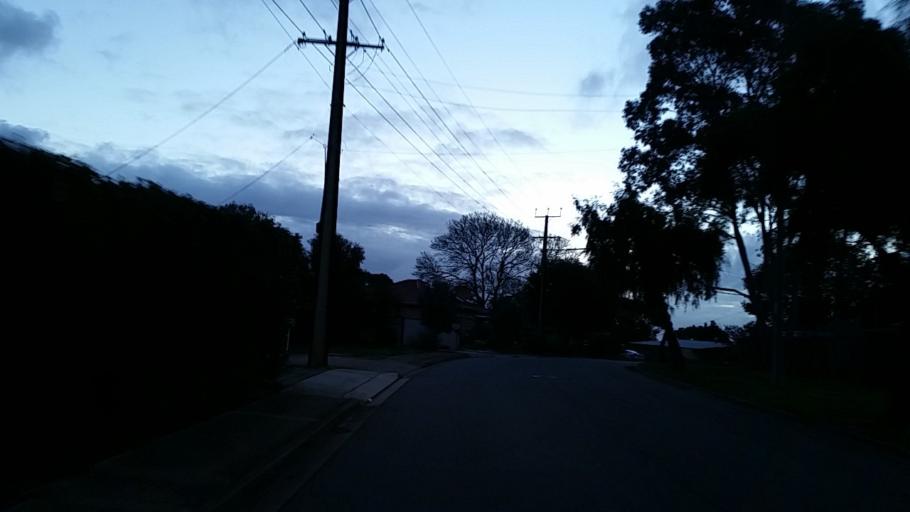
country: AU
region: South Australia
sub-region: Tea Tree Gully
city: Hope Valley
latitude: -34.8252
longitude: 138.7038
